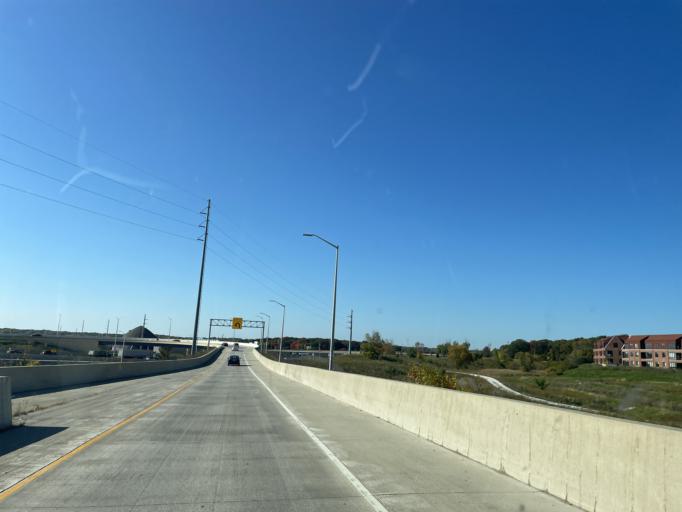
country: US
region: Wisconsin
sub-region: Milwaukee County
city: Wauwatosa
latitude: 43.0469
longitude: -88.0351
